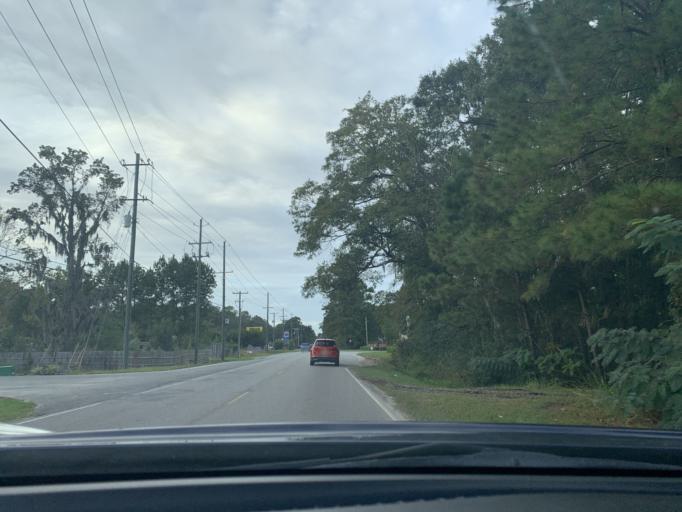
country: US
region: Georgia
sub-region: Chatham County
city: Pooler
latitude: 32.0533
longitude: -81.2669
